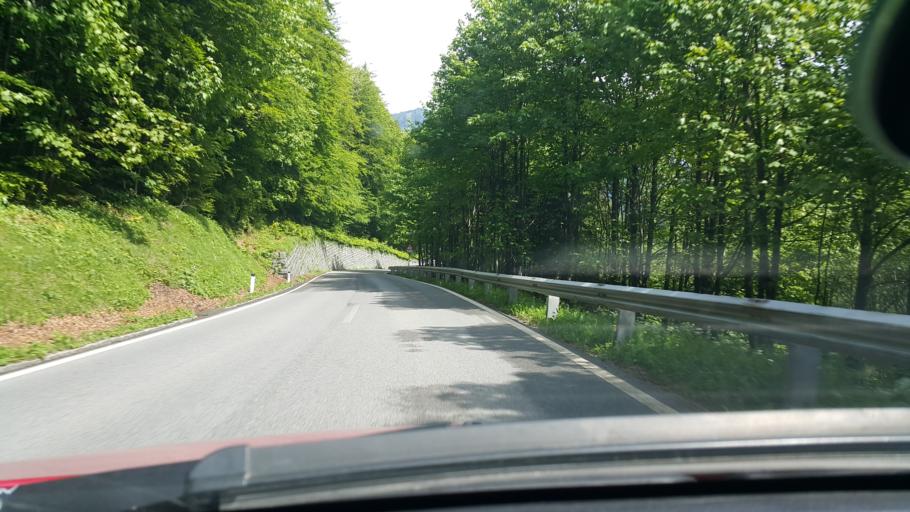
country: AT
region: Carinthia
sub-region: Politischer Bezirk Klagenfurt Land
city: Ferlach
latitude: 46.4493
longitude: 14.2556
